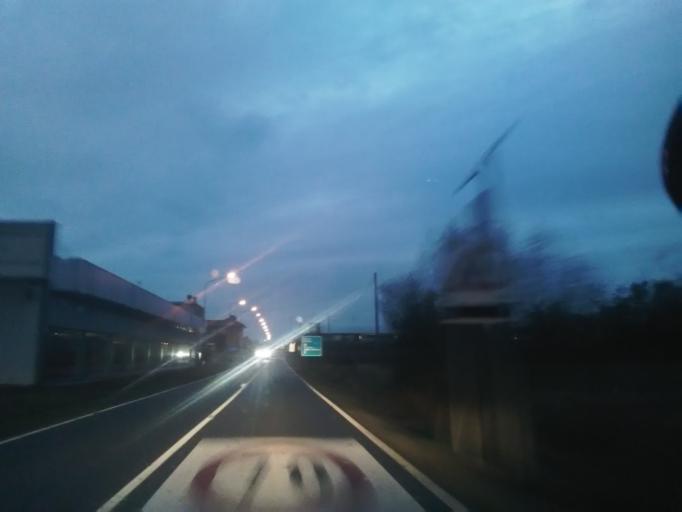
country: IT
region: Piedmont
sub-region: Provincia di Vercelli
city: Lozzolo
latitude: 45.6093
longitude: 8.3285
